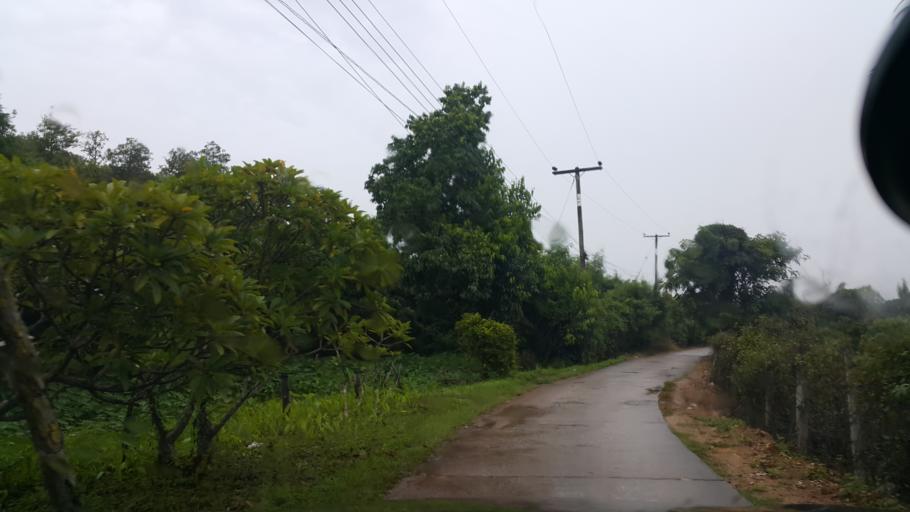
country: TH
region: Lamphun
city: Ban Thi
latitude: 18.6154
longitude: 99.1177
